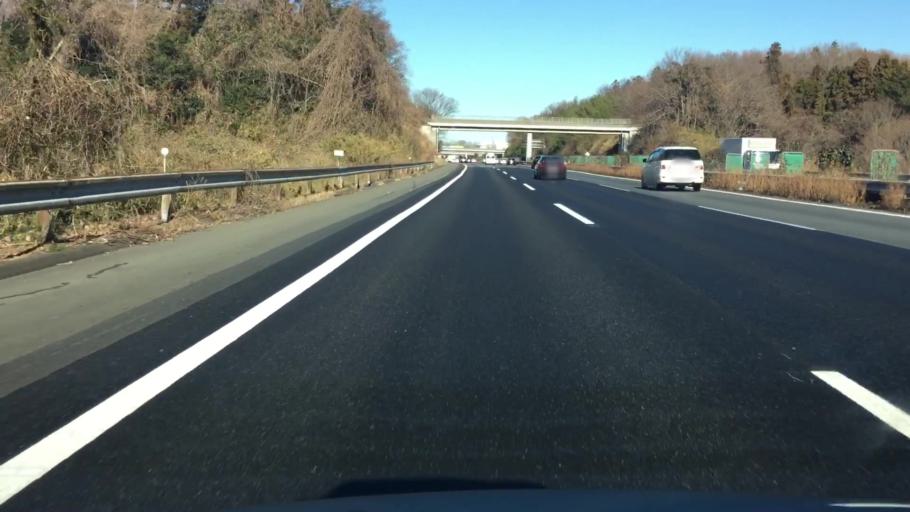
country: JP
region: Saitama
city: Ogawa
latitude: 36.0960
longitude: 139.2840
